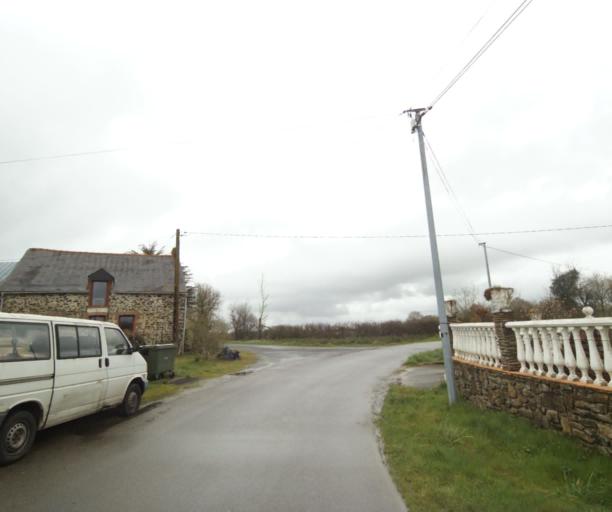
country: FR
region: Pays de la Loire
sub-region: Departement de la Loire-Atlantique
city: Quilly
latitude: 47.4532
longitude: -1.8975
